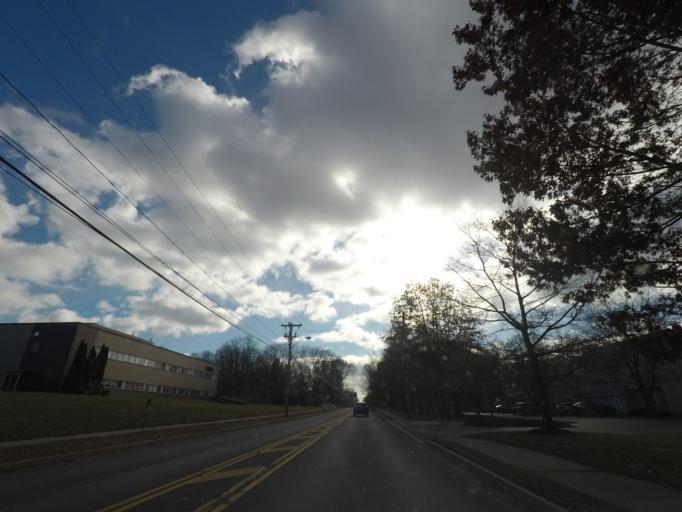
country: US
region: New York
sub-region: Schenectady County
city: Schenectady
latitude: 42.8137
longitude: -73.8926
